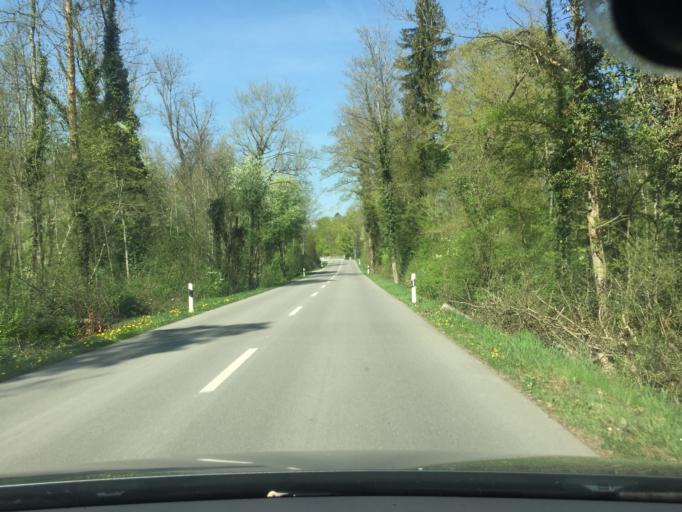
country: DE
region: Baden-Wuerttemberg
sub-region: Freiburg Region
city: Lottstetten
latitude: 47.5917
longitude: 8.6063
